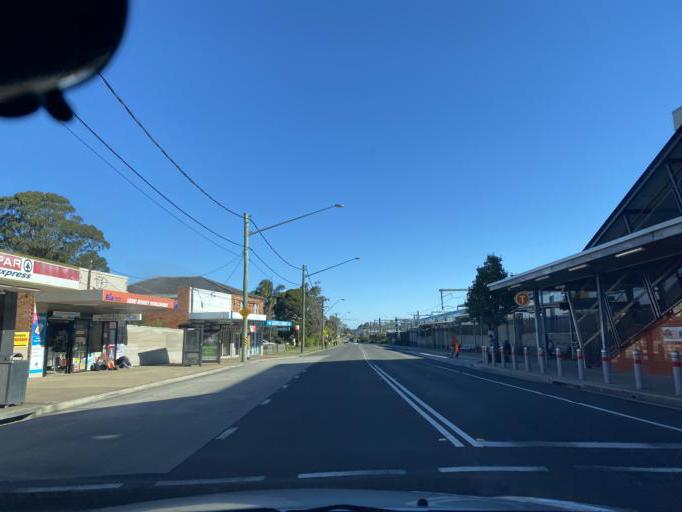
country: AU
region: New South Wales
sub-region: Campbelltown Municipality
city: Glenfield
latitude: -33.9724
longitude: 150.8934
